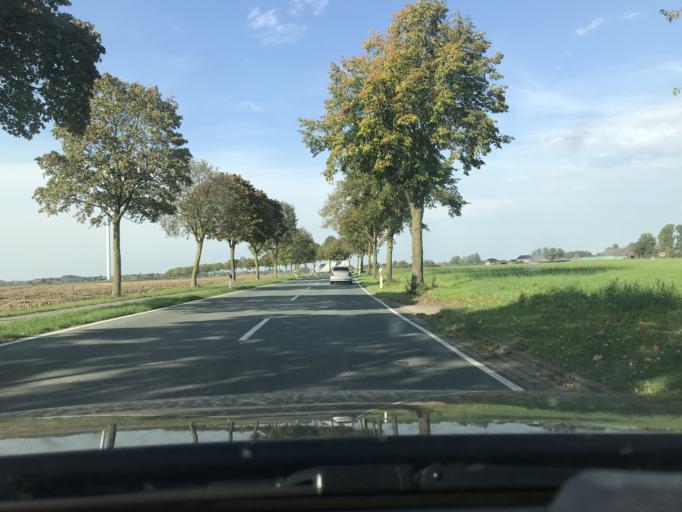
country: DE
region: North Rhine-Westphalia
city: Kalkar
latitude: 51.7696
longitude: 6.2504
